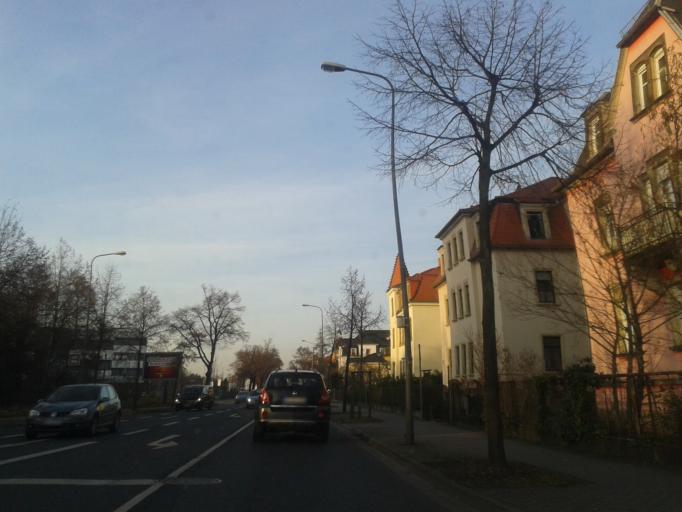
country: DE
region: Saxony
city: Heidenau
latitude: 51.0136
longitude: 13.8110
